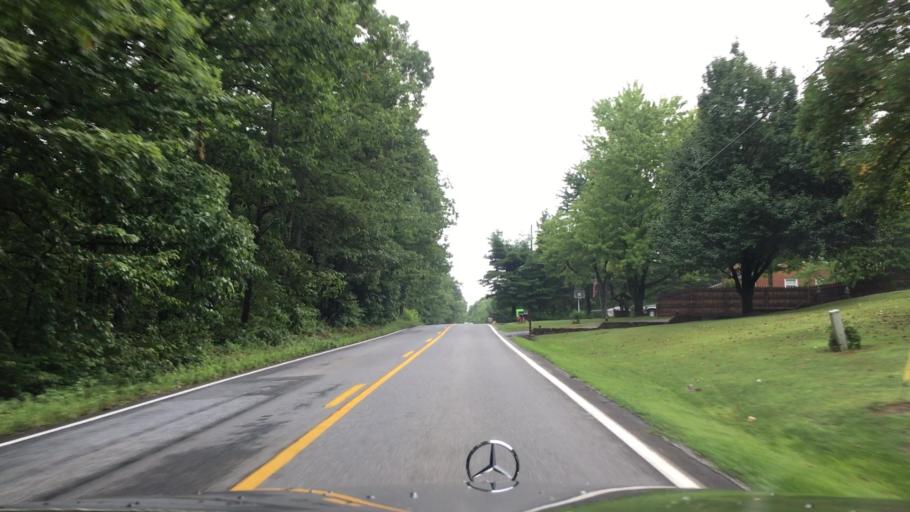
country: US
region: Virginia
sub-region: Campbell County
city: Timberlake
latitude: 37.2693
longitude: -79.2606
